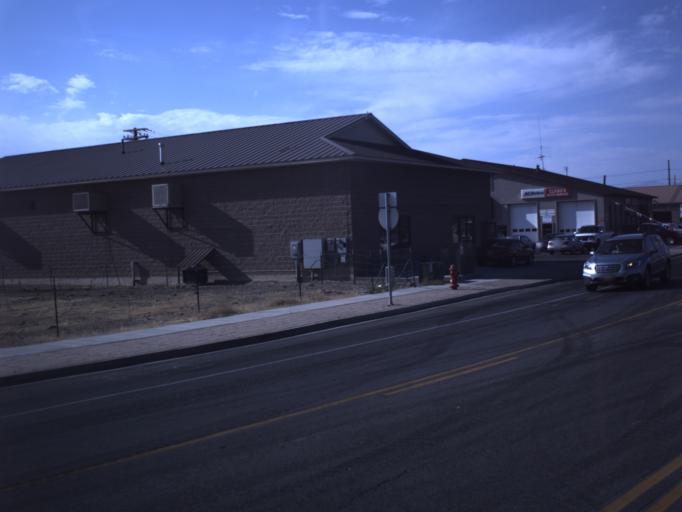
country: US
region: Utah
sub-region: Utah County
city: Spanish Fork
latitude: 40.1277
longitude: -111.6547
